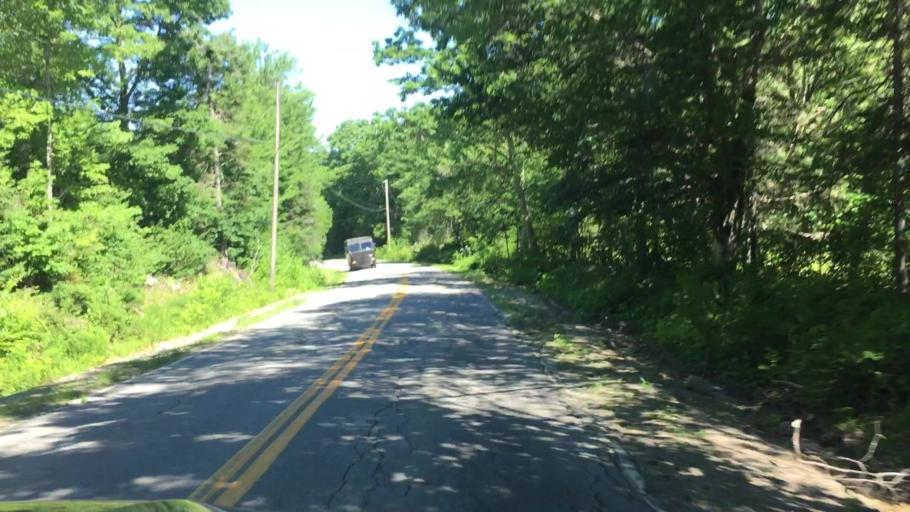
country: US
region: Maine
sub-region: Hancock County
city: Penobscot
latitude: 44.4227
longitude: -68.7062
